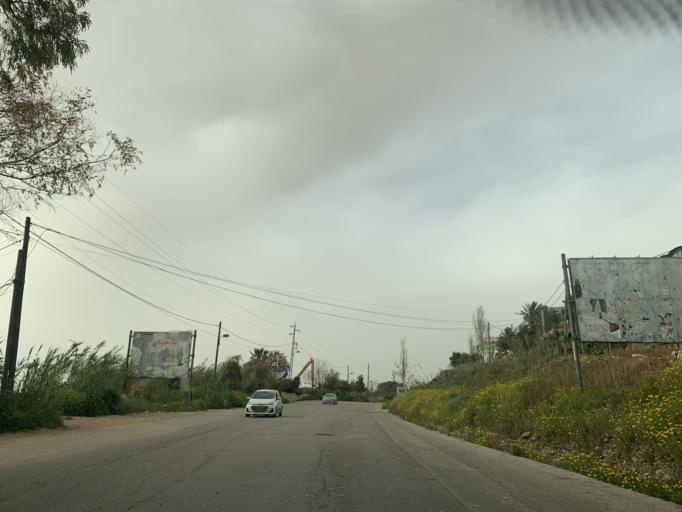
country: LB
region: Mont-Liban
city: Jbail
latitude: 34.1062
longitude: 35.6518
